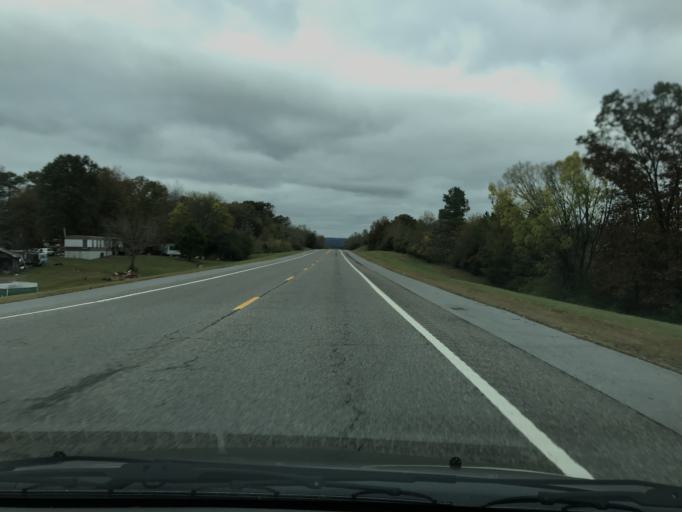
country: US
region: Tennessee
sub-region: Rhea County
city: Graysville
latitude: 35.3923
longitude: -85.0080
